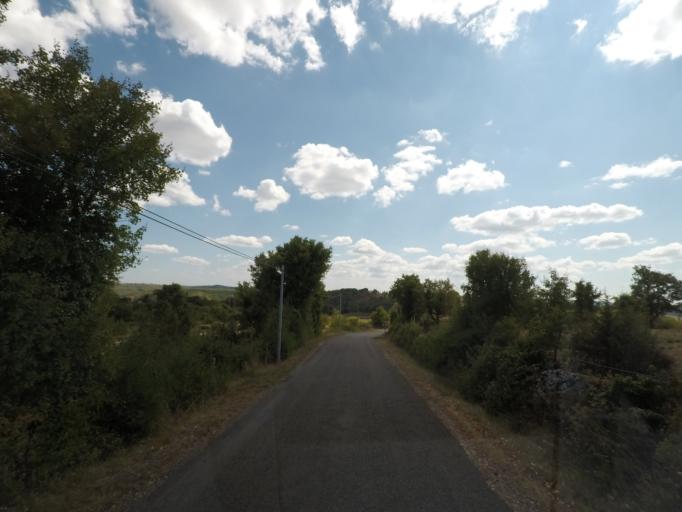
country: FR
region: Midi-Pyrenees
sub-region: Departement du Lot
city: Cajarc
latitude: 44.5252
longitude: 1.6608
